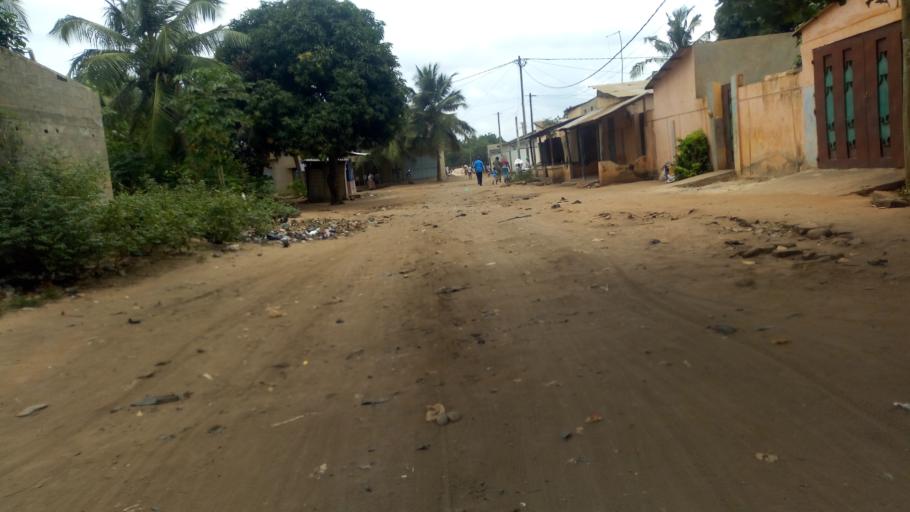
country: TG
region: Maritime
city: Lome
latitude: 6.2336
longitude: 1.1831
